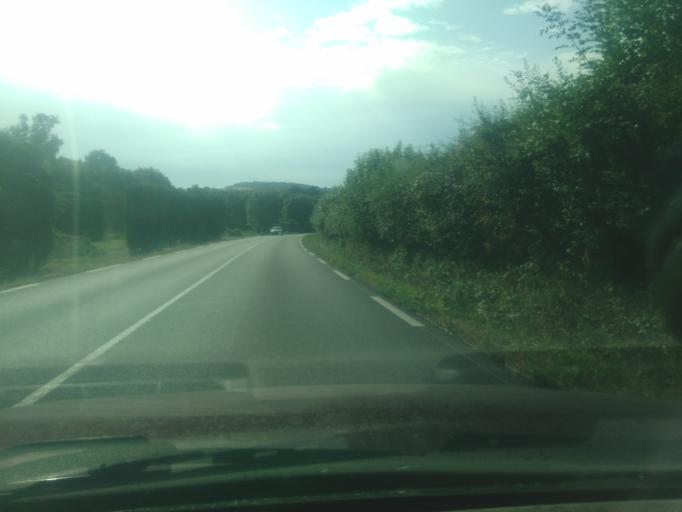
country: FR
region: Pays de la Loire
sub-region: Departement de la Vendee
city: Mouilleron-en-Pareds
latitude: 46.6726
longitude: -0.8105
